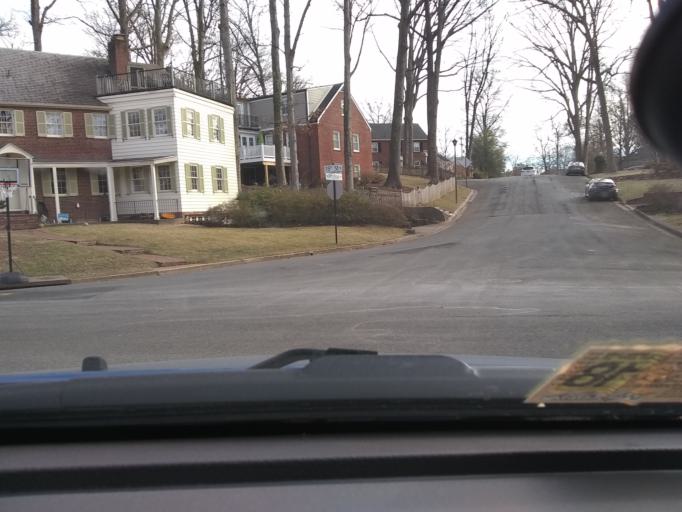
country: US
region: Virginia
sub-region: Fairfax County
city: Seven Corners
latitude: 38.8852
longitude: -77.1335
